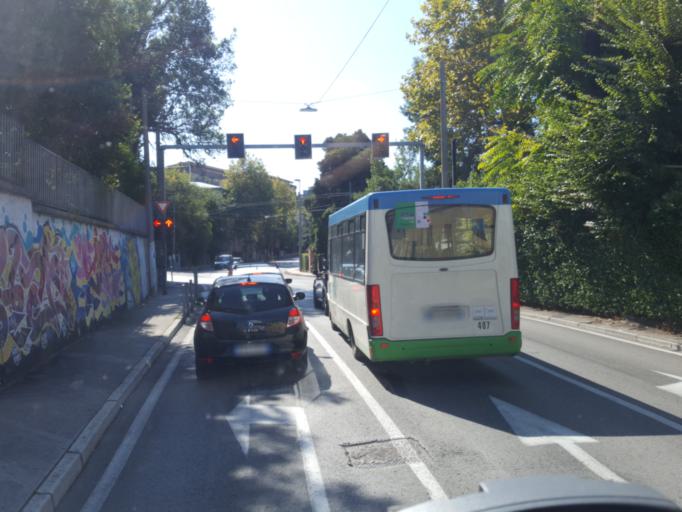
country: IT
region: The Marches
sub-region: Provincia di Ancona
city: Le Grazie di Ancona
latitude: 43.5988
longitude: 13.5165
